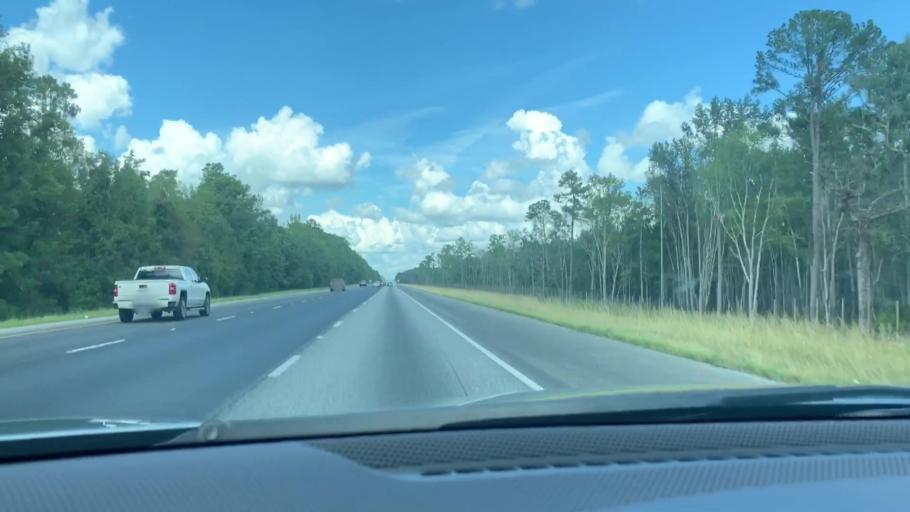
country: US
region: Georgia
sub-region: Camden County
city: Woodbine
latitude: 30.8943
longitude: -81.6857
